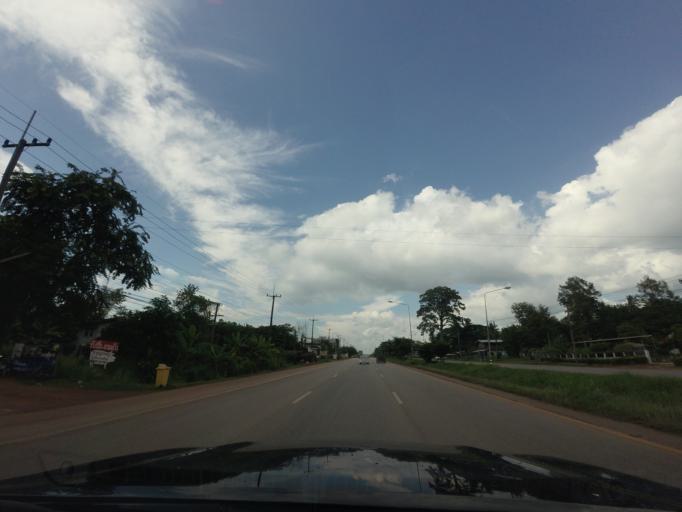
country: TH
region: Changwat Udon Thani
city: Udon Thani
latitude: 17.5455
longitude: 102.8005
